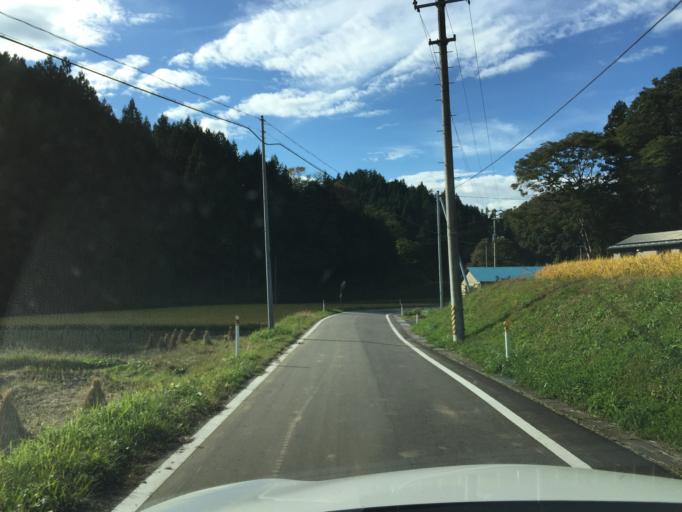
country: JP
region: Fukushima
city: Ishikawa
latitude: 37.1667
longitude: 140.4986
